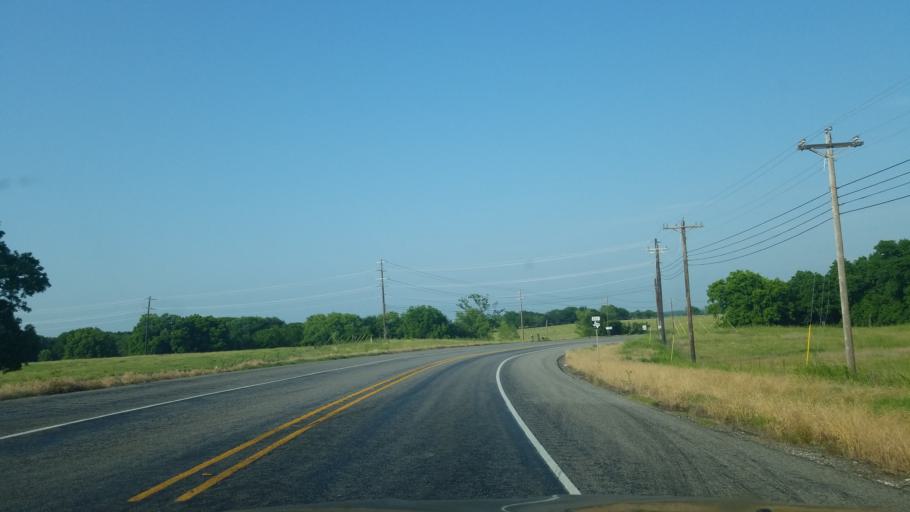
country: US
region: Texas
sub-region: Denton County
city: Krugerville
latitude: 33.3065
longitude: -97.0623
